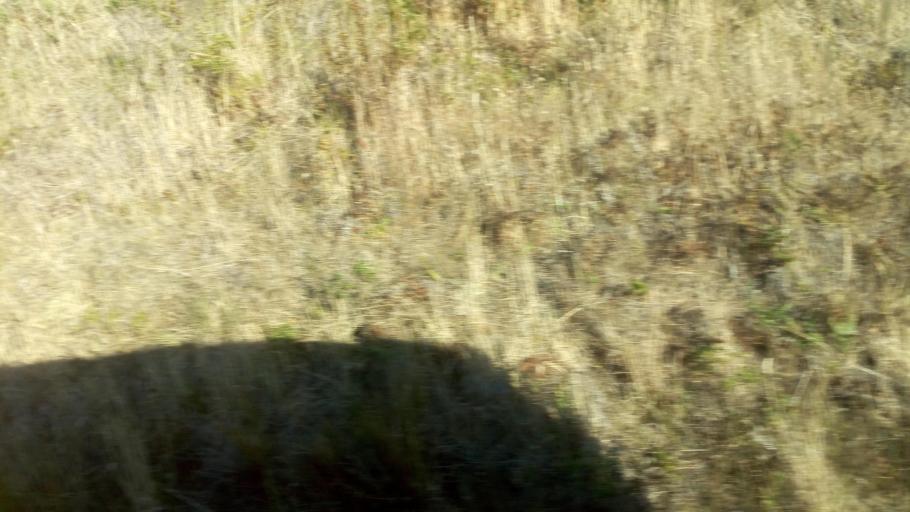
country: US
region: California
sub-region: Marin County
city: Inverness
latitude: 38.0414
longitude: -122.8728
